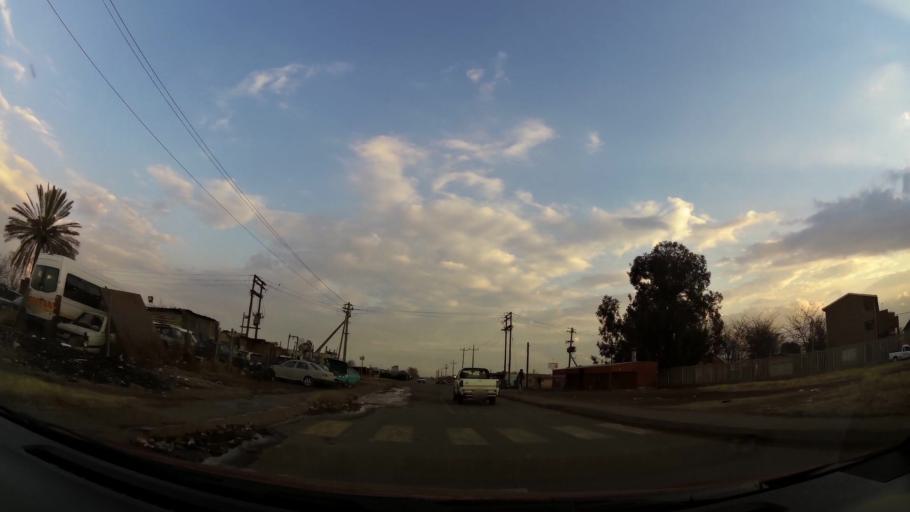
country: ZA
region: Gauteng
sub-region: City of Johannesburg Metropolitan Municipality
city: Orange Farm
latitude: -26.5455
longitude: 27.8426
